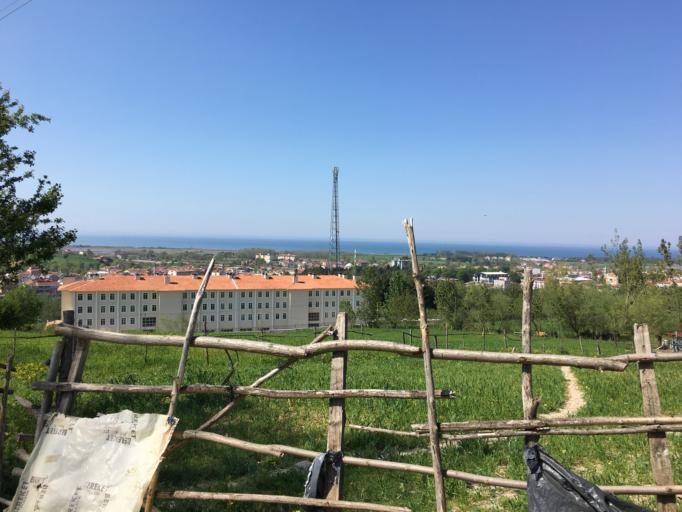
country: TR
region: Samsun
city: Alacam
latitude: 41.6067
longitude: 35.6048
